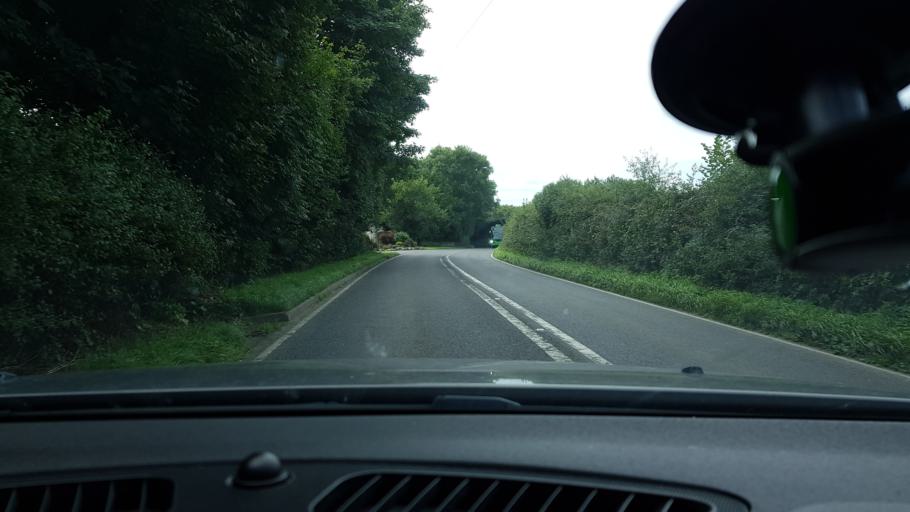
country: GB
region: England
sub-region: Cornwall
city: Camelford
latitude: 50.5973
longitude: -4.7117
